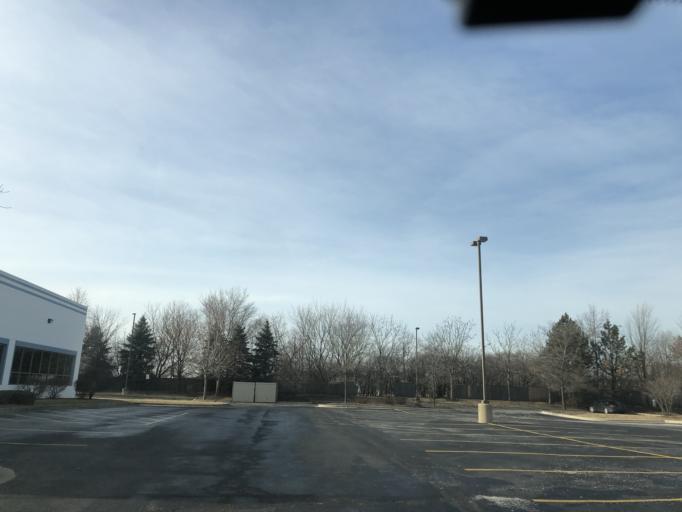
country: US
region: Illinois
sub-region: Cook County
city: Lemont
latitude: 41.7192
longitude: -88.0098
